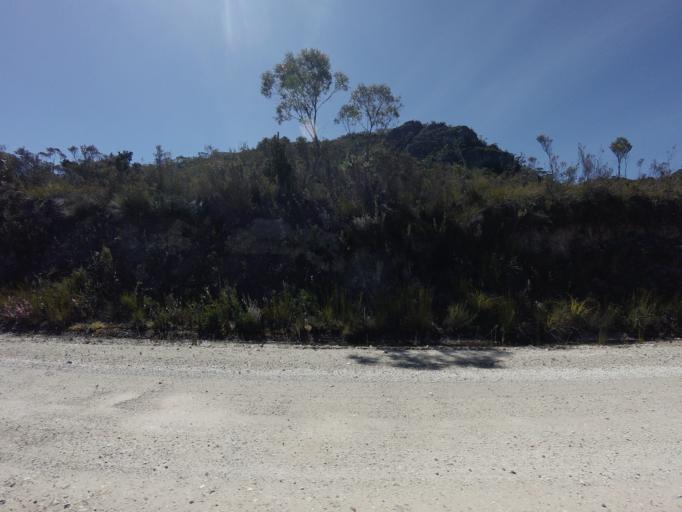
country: AU
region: Tasmania
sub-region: Huon Valley
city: Geeveston
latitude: -42.9435
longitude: 146.3490
